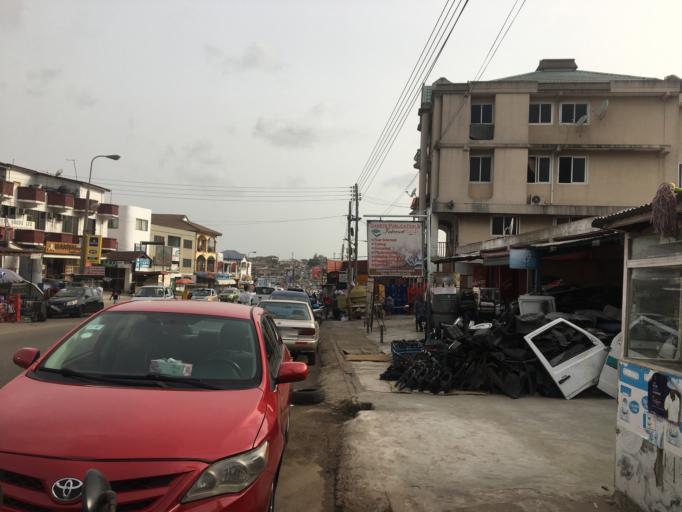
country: GH
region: Greater Accra
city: Accra
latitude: 5.5913
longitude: -0.1958
